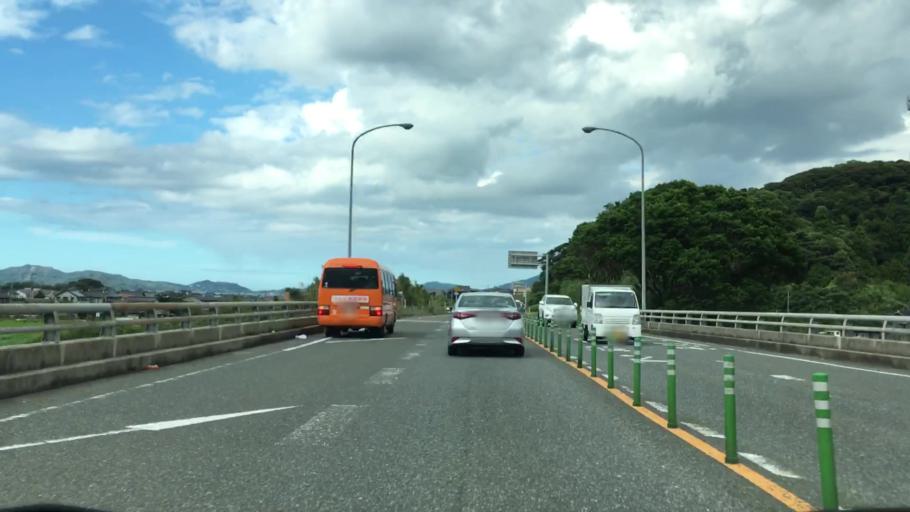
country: JP
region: Saga Prefecture
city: Karatsu
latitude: 33.4971
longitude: 130.0801
